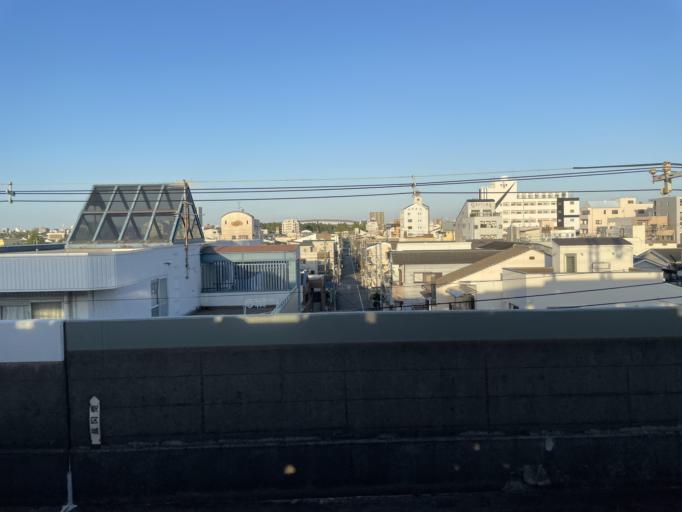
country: JP
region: Osaka
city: Matsubara
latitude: 34.6157
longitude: 135.5331
